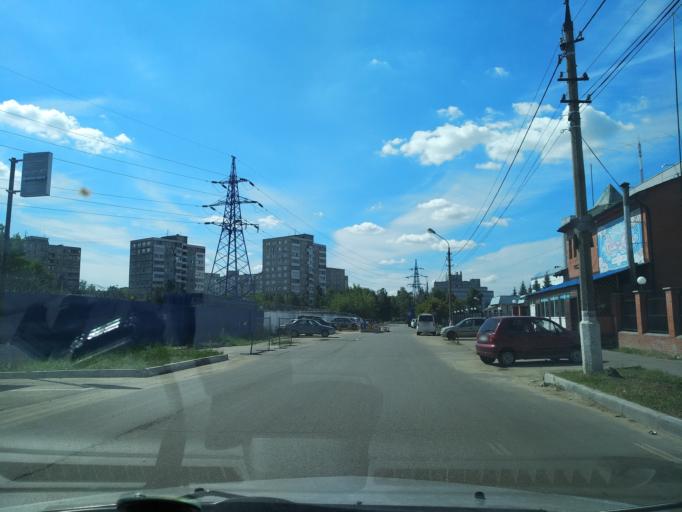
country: RU
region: Moskovskaya
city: Zhukovskiy
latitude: 55.6039
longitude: 38.1118
